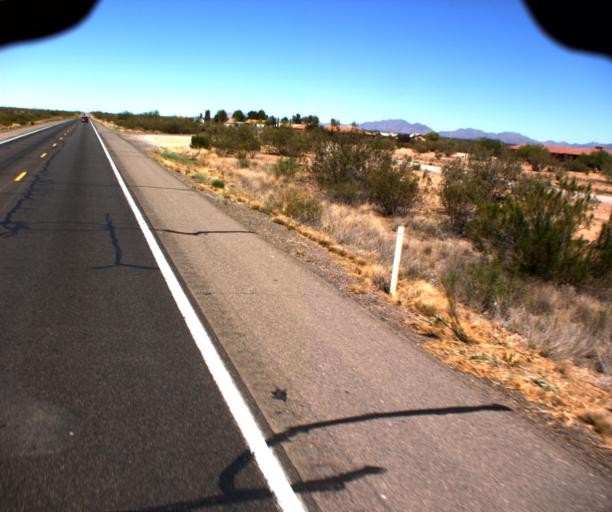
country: US
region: Arizona
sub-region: Yavapai County
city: Congress
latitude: 34.0405
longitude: -112.8314
